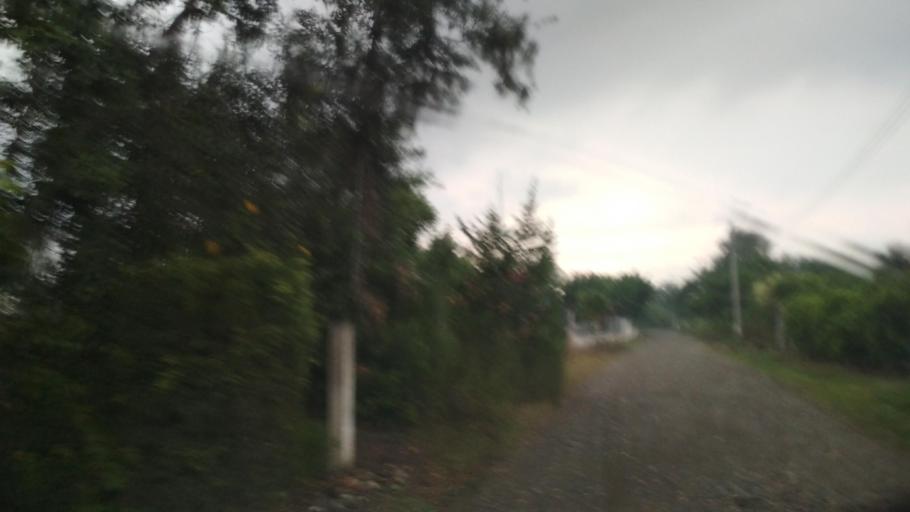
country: MM
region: Shan
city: Taunggyi
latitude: 20.3011
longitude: 97.3066
